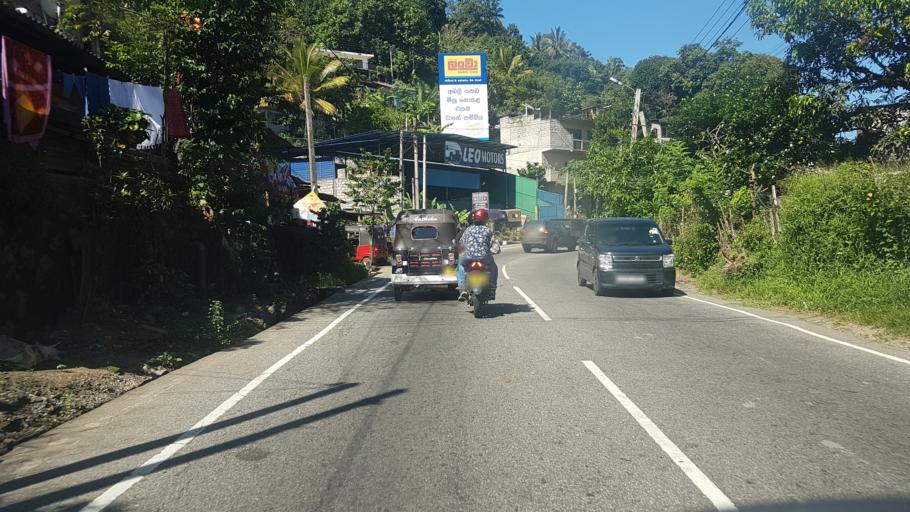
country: LK
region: Central
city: Kandy
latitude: 7.2870
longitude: 80.6588
